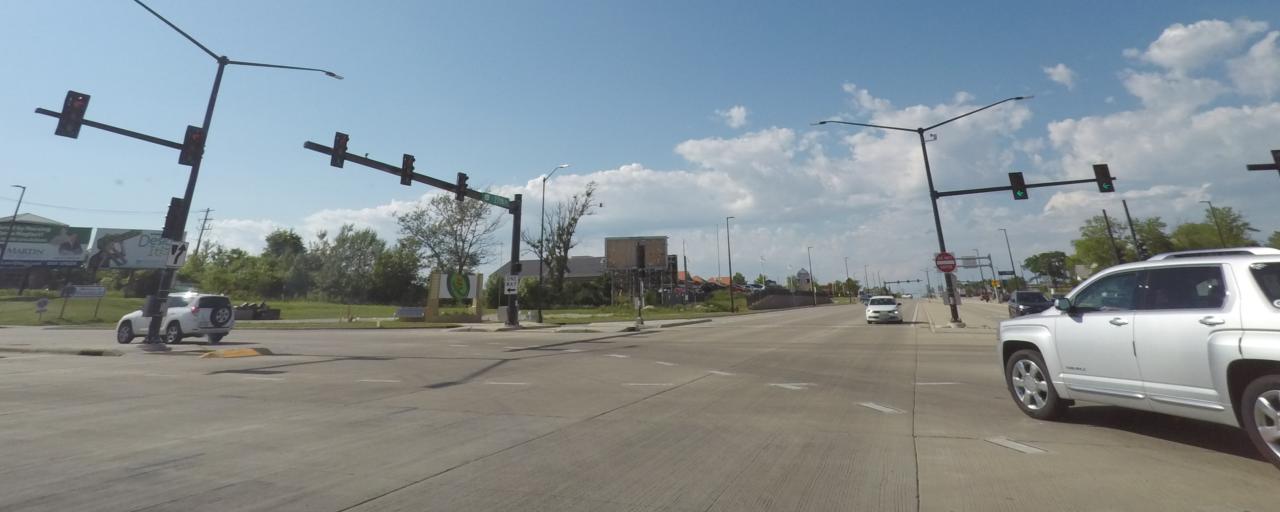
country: US
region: Wisconsin
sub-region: Milwaukee County
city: Greendale
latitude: 42.9164
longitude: -87.9500
